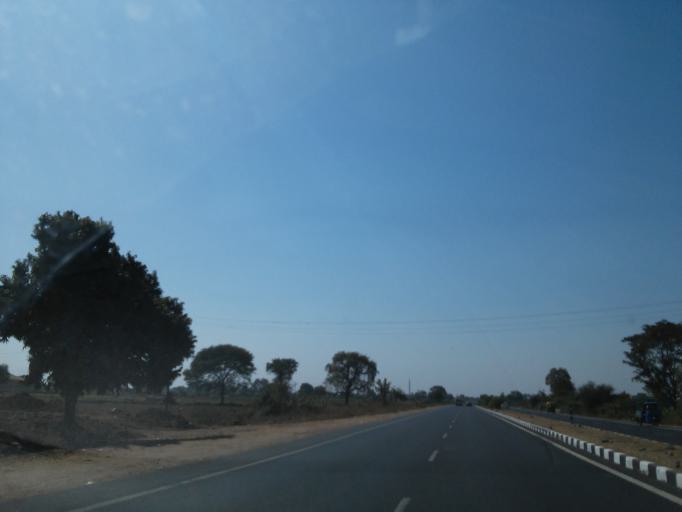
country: IN
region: Gujarat
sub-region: Sabar Kantha
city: Himatnagar
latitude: 23.4819
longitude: 72.8909
